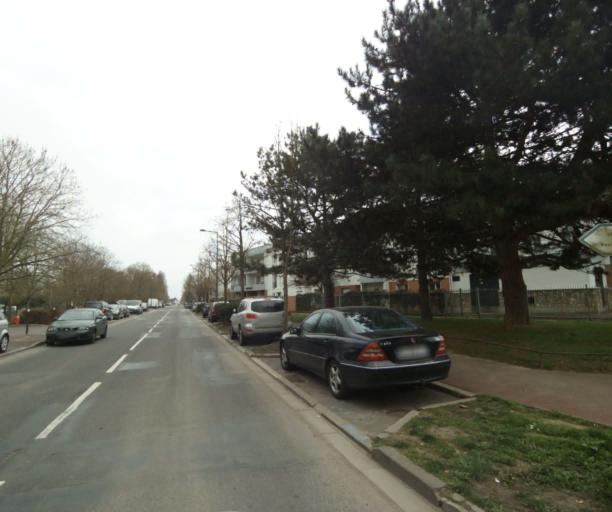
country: FR
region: Ile-de-France
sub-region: Departement du Val-d'Oise
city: Vaureal
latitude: 49.0509
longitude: 2.0389
